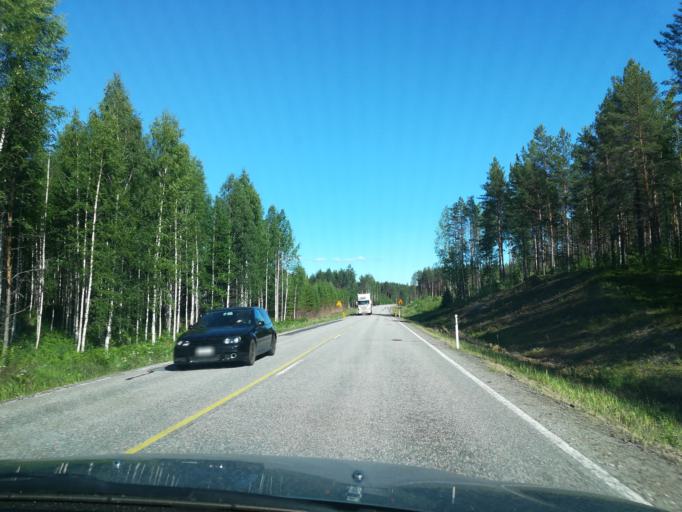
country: FI
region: Southern Savonia
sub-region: Mikkeli
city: Puumala
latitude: 61.4712
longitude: 28.3062
